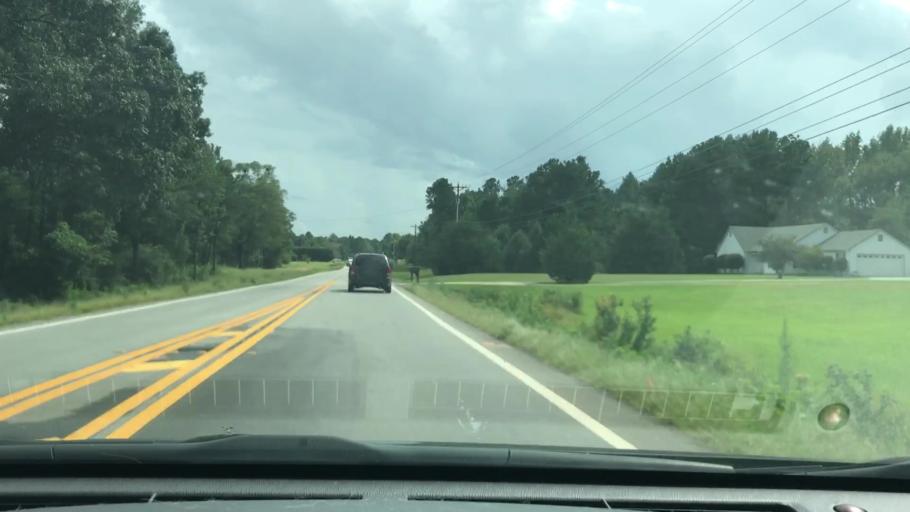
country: US
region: Georgia
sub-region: Walton County
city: Walnut Grove
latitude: 33.7554
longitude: -83.8522
